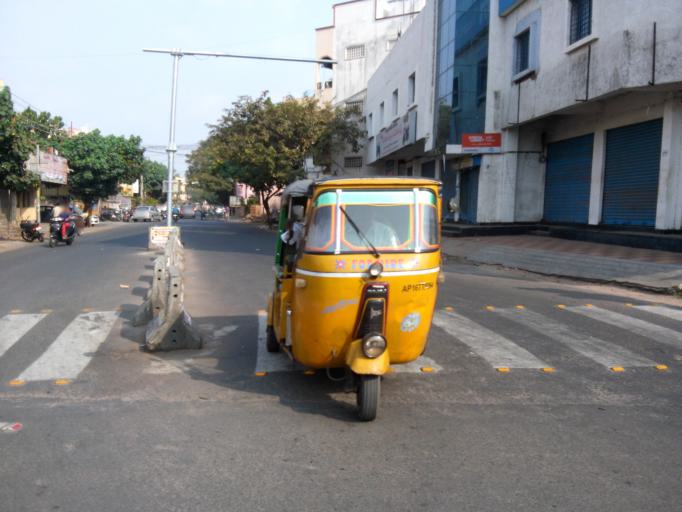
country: IN
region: Andhra Pradesh
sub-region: Krishna
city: Vijayawada
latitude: 16.5159
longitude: 80.6392
